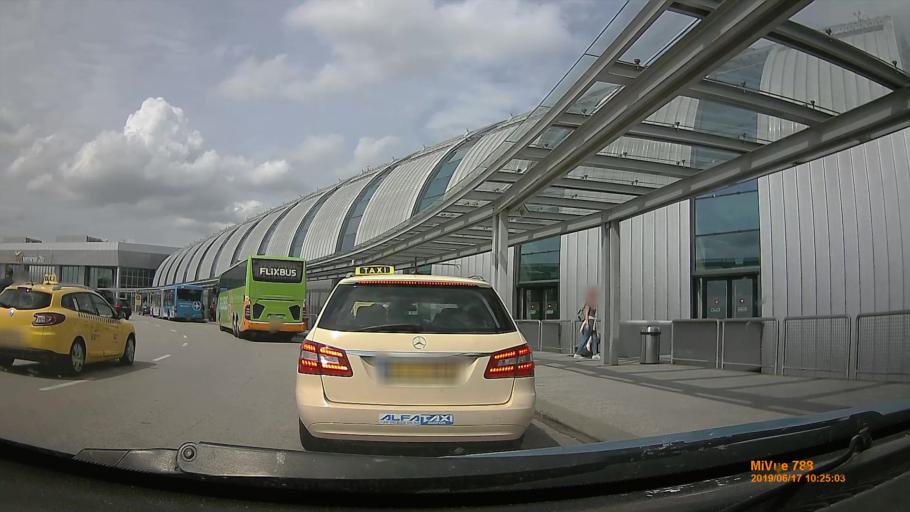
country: HU
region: Pest
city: Vecses
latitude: 47.4326
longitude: 19.2619
